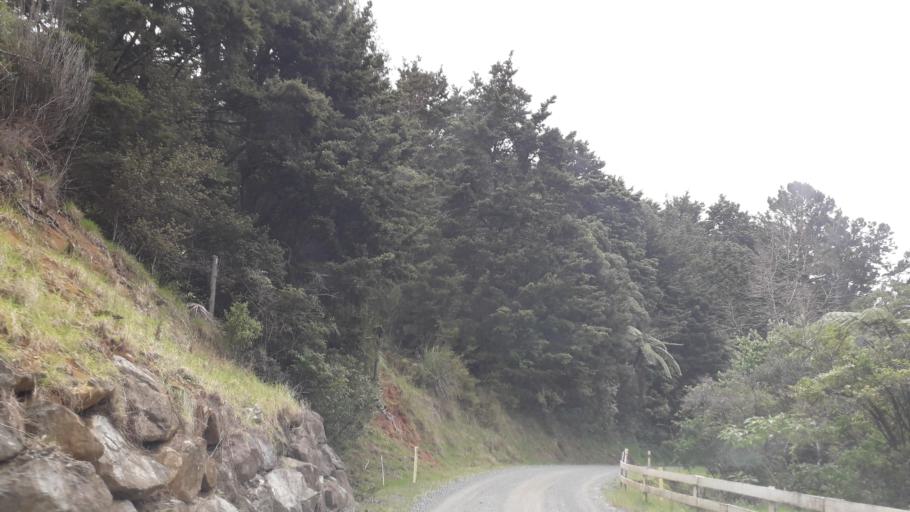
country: NZ
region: Northland
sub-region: Far North District
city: Taipa
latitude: -35.0753
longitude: 173.5537
